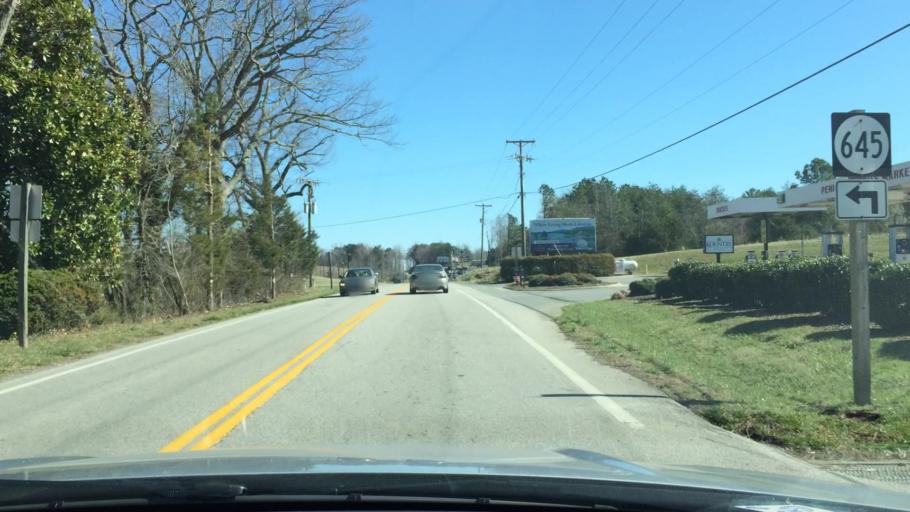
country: US
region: Virginia
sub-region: Franklin County
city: Union Hall
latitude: 36.9811
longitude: -79.6251
